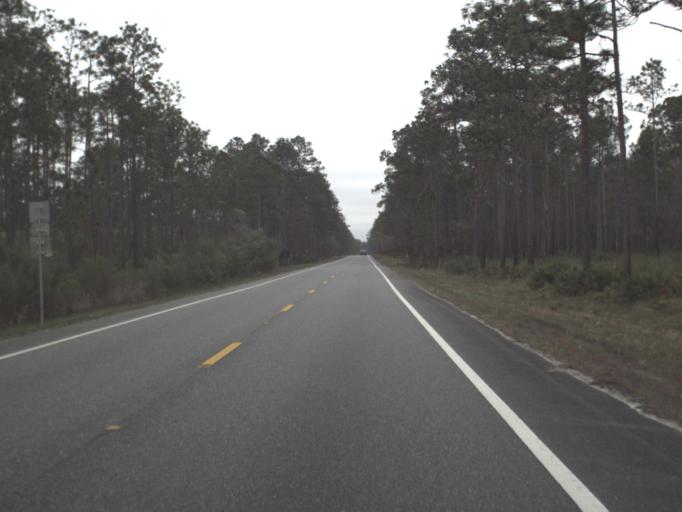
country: US
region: Florida
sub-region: Gulf County
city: Wewahitchka
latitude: 29.9911
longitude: -84.9766
